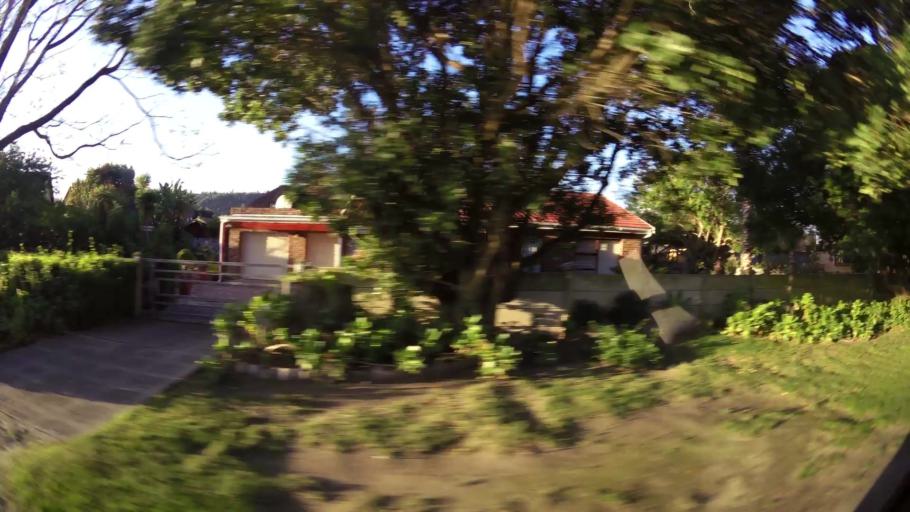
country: ZA
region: Western Cape
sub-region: Eden District Municipality
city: Knysna
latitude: -34.0145
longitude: 22.7827
